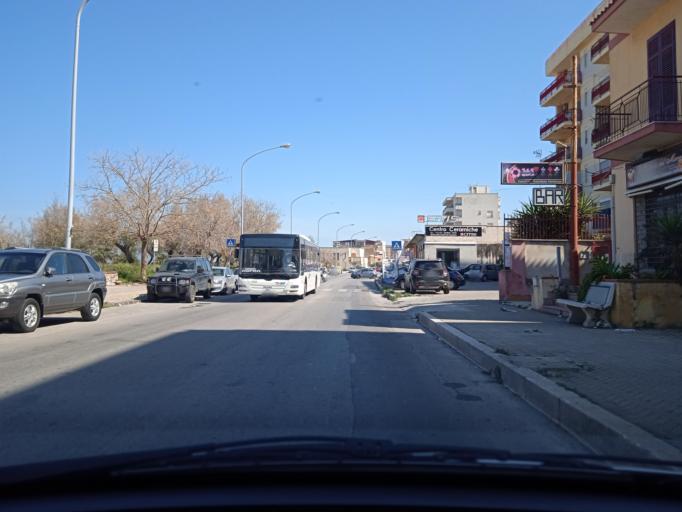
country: IT
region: Sicily
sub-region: Palermo
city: Ciaculli
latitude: 38.1001
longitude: 13.4028
